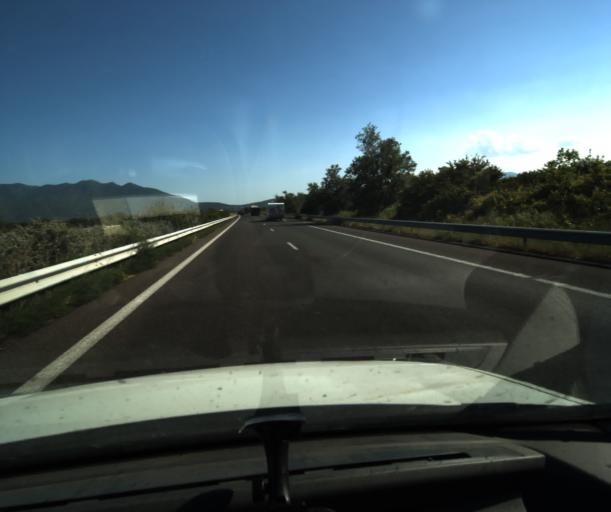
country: FR
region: Languedoc-Roussillon
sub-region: Departement des Pyrenees-Orientales
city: Villemolaque
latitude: 42.5682
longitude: 2.8437
